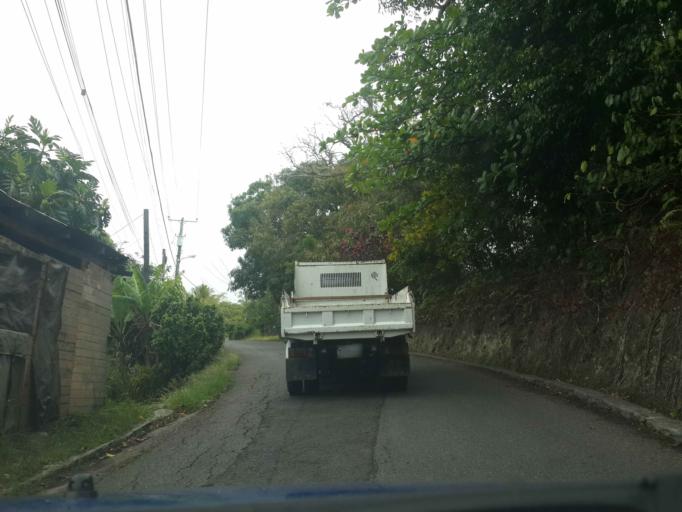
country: LC
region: Castries Quarter
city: Castries
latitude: 13.9949
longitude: -60.9809
